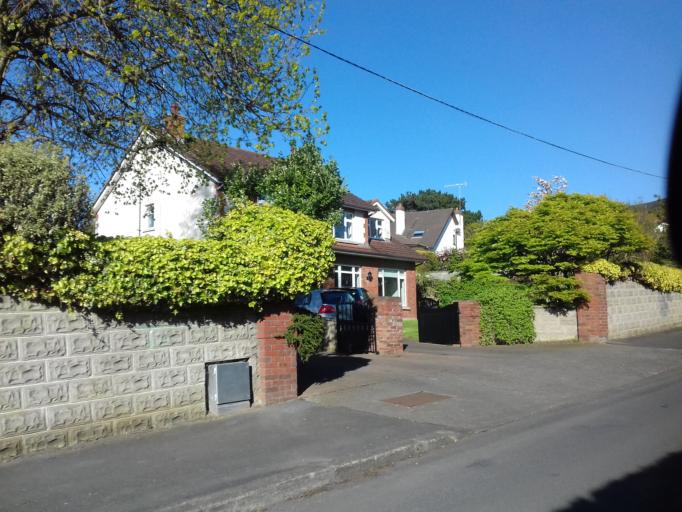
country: IE
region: Leinster
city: Sutton
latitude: 53.3751
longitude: -6.0940
